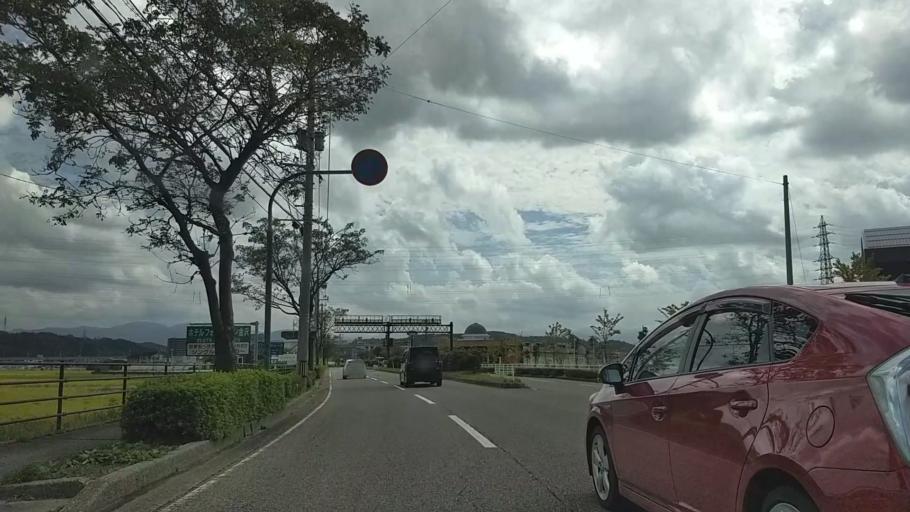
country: JP
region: Ishikawa
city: Kanazawa-shi
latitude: 36.5985
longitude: 136.6600
